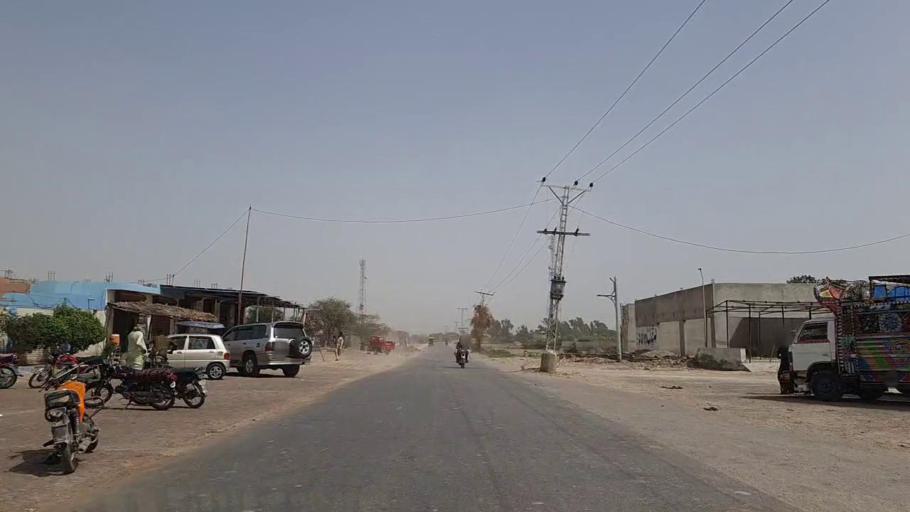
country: PK
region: Sindh
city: Talhar
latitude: 24.8831
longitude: 68.8244
